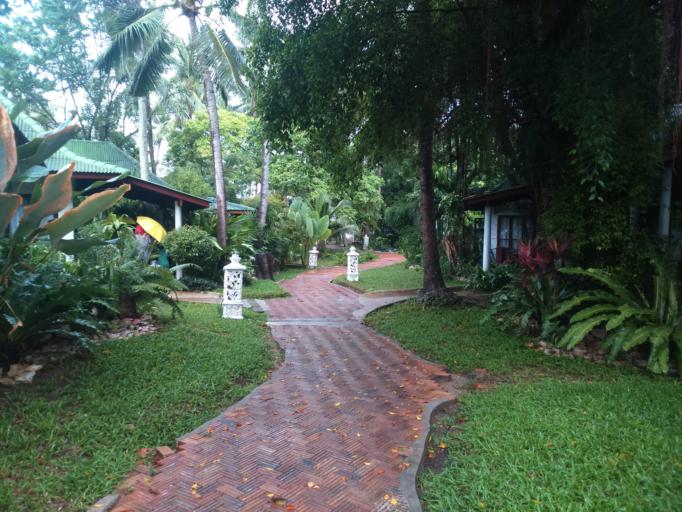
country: TH
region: Surat Thani
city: Ko Samui
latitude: 9.4767
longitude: 100.0667
